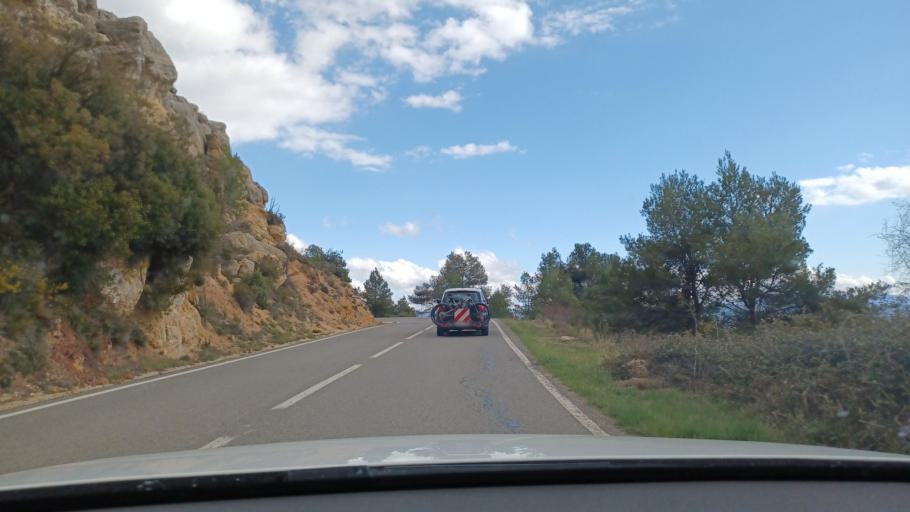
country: ES
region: Catalonia
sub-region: Provincia de Tarragona
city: la Morera de Montsant
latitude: 41.2694
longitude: 0.8535
